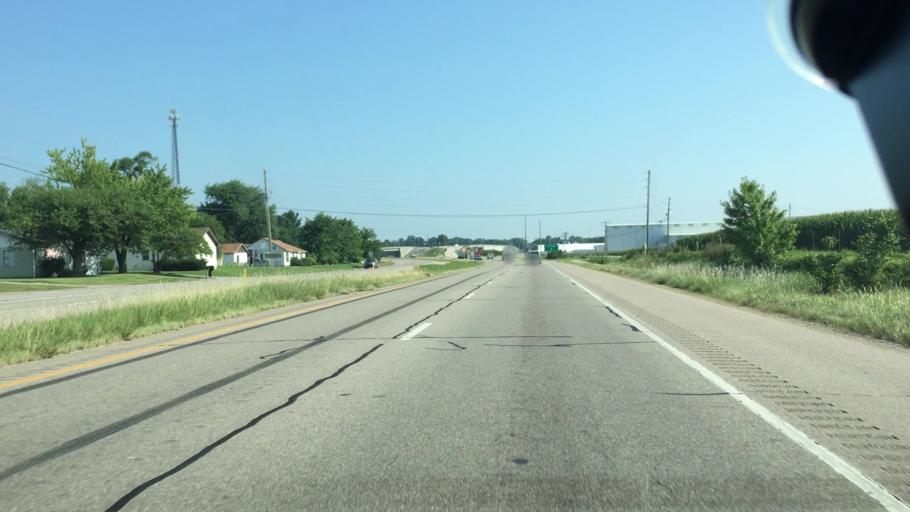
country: US
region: Indiana
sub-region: Gibson County
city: Princeton
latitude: 38.3062
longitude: -87.5673
